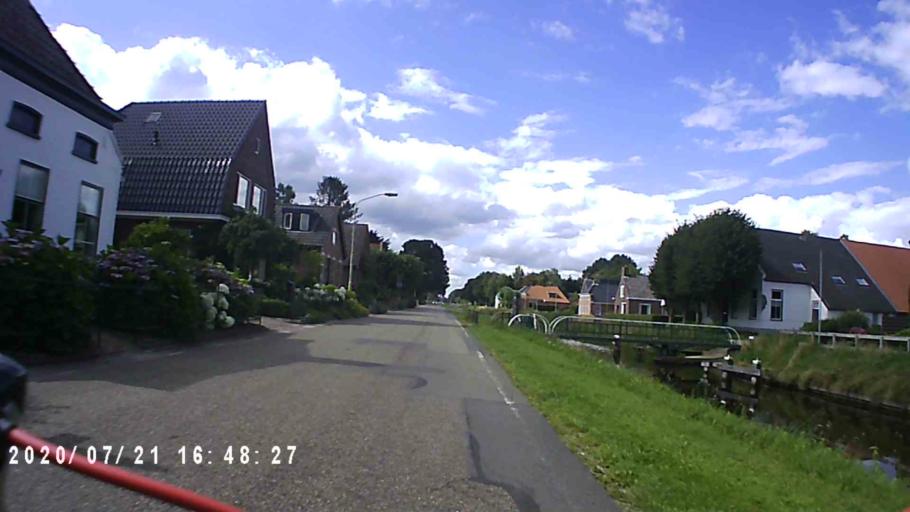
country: NL
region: Groningen
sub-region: Gemeente Hoogezand-Sappemeer
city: Hoogezand
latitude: 53.1168
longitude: 6.7759
